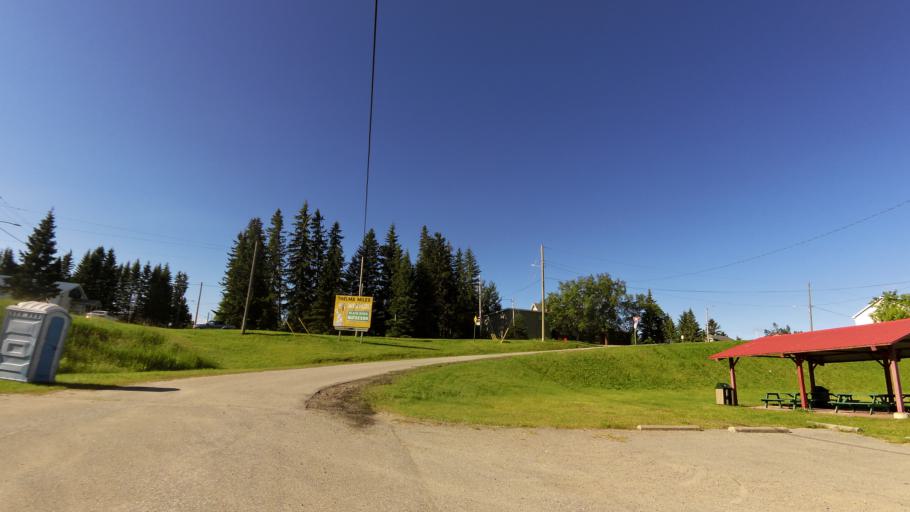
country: CA
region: Ontario
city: Iroquois Falls
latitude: 48.5381
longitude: -80.4643
